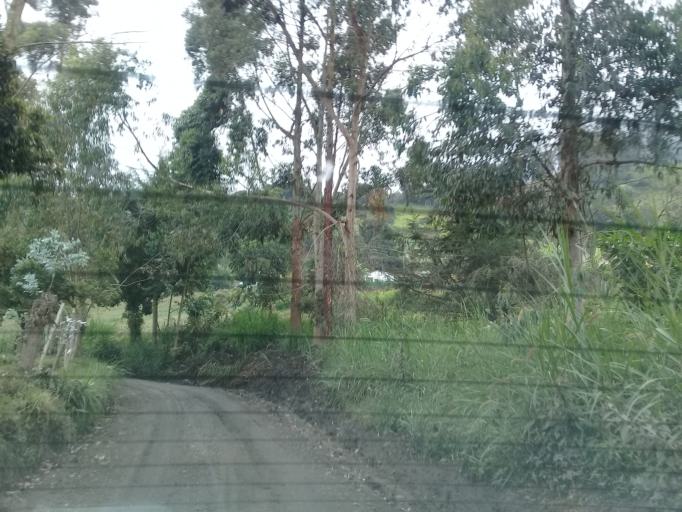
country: CO
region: Cundinamarca
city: Une
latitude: 4.4001
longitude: -73.9894
